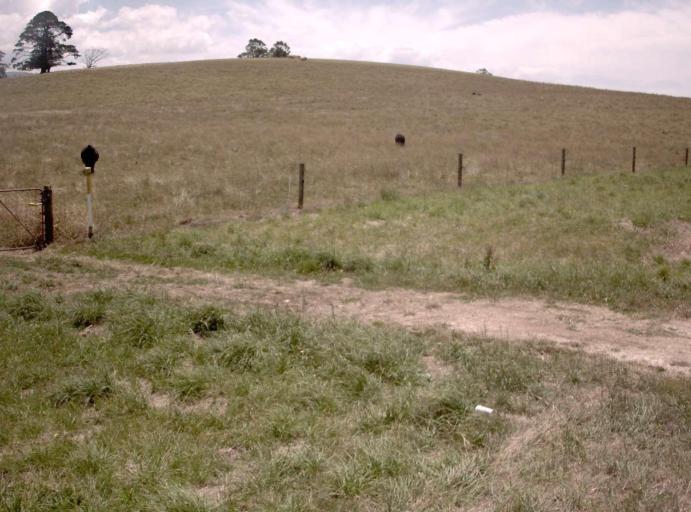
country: AU
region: Victoria
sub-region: Latrobe
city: Moe
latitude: -38.0164
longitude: 146.3670
